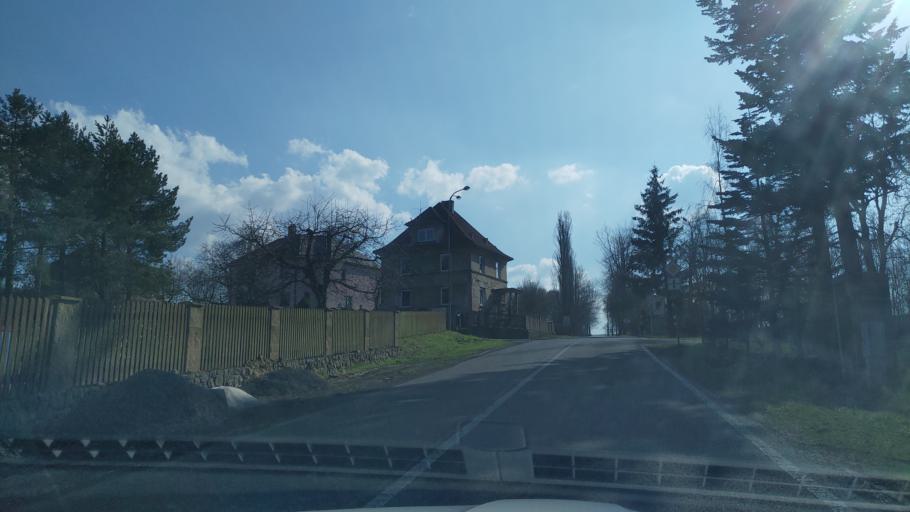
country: CZ
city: Kamenicky Senov
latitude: 50.7711
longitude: 14.4688
